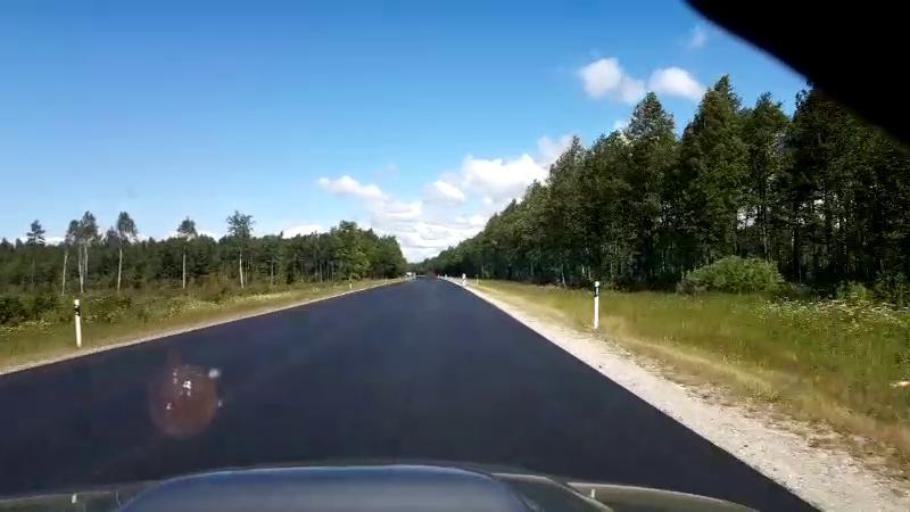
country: LV
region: Salacgrivas
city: Ainazi
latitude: 58.0168
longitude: 24.4961
